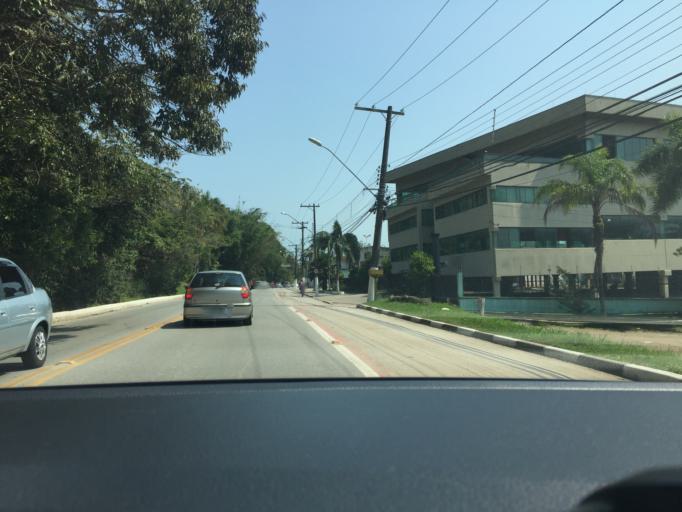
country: BR
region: Sao Paulo
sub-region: Guaruja
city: Guaruja
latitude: -23.9832
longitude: -46.1984
